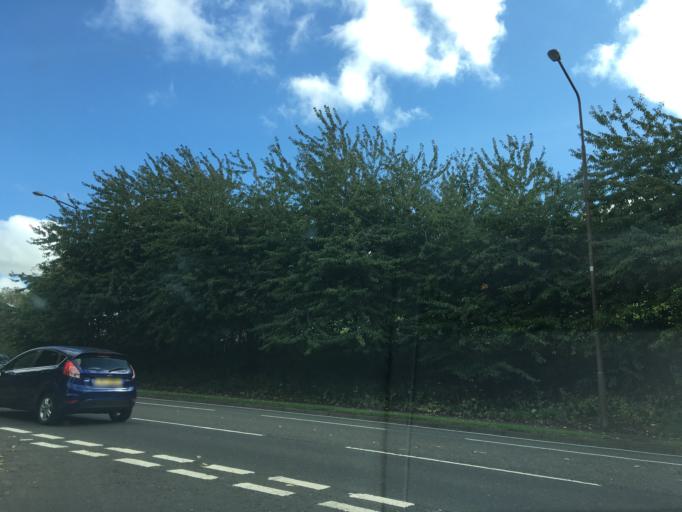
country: GB
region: Scotland
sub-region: West Lothian
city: Linlithgow
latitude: 55.9836
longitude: -3.5845
